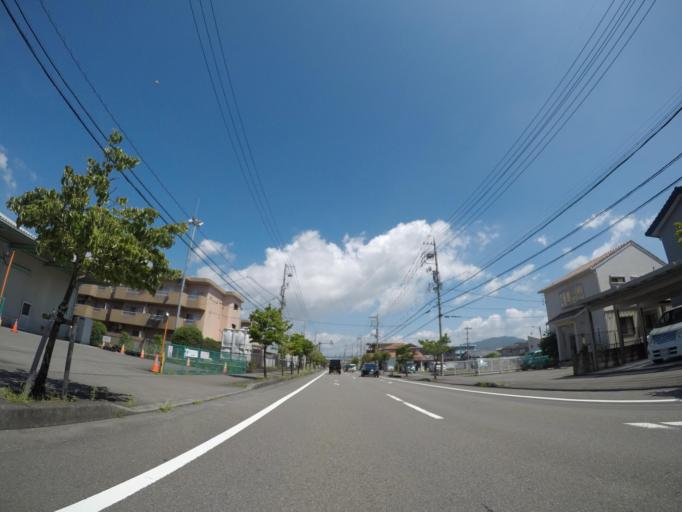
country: JP
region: Shizuoka
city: Fujieda
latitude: 34.8568
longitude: 138.2885
